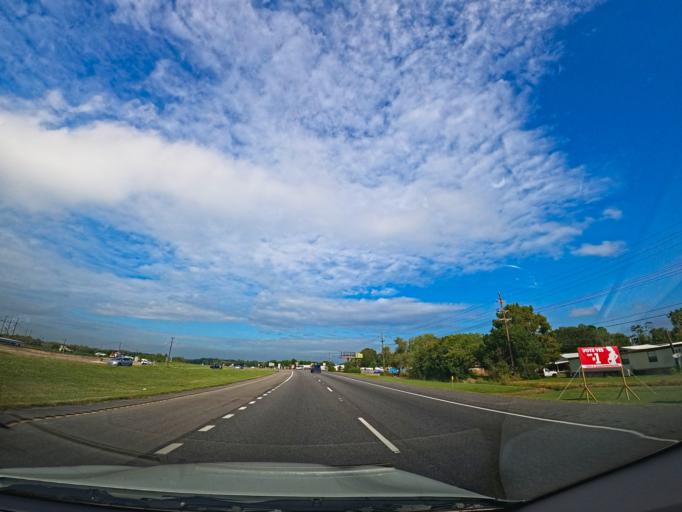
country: US
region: Louisiana
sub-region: Saint Mary Parish
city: Patterson
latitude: 29.6877
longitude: -91.3064
